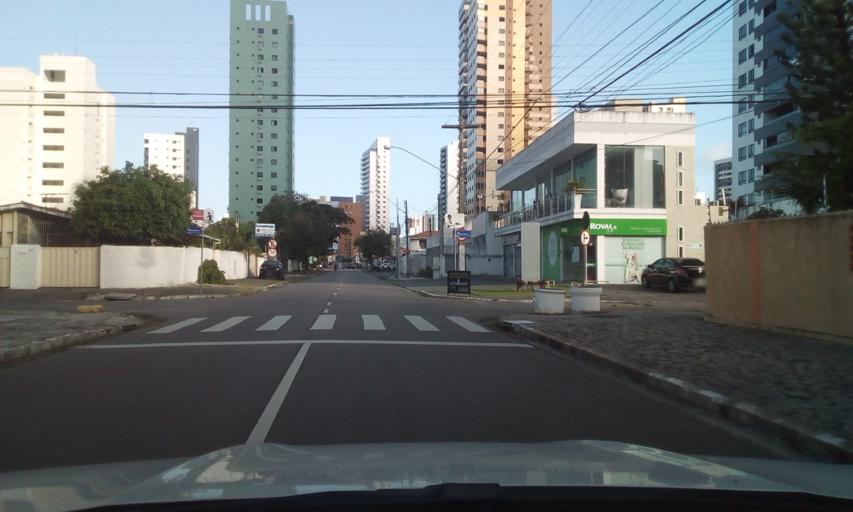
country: BR
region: Paraiba
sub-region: Joao Pessoa
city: Joao Pessoa
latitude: -7.1046
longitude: -34.8346
